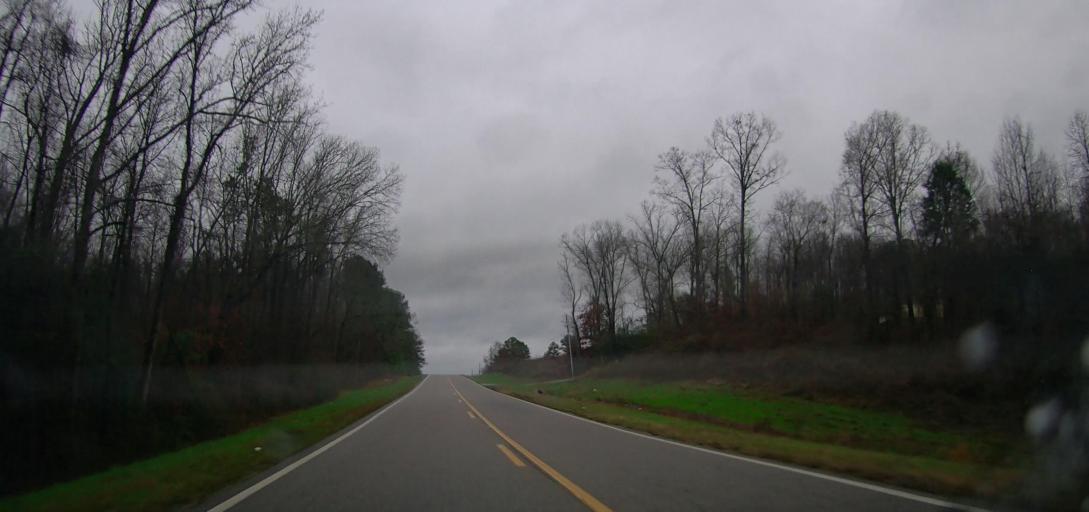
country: US
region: Alabama
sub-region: Bibb County
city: Centreville
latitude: 32.8416
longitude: -86.9578
